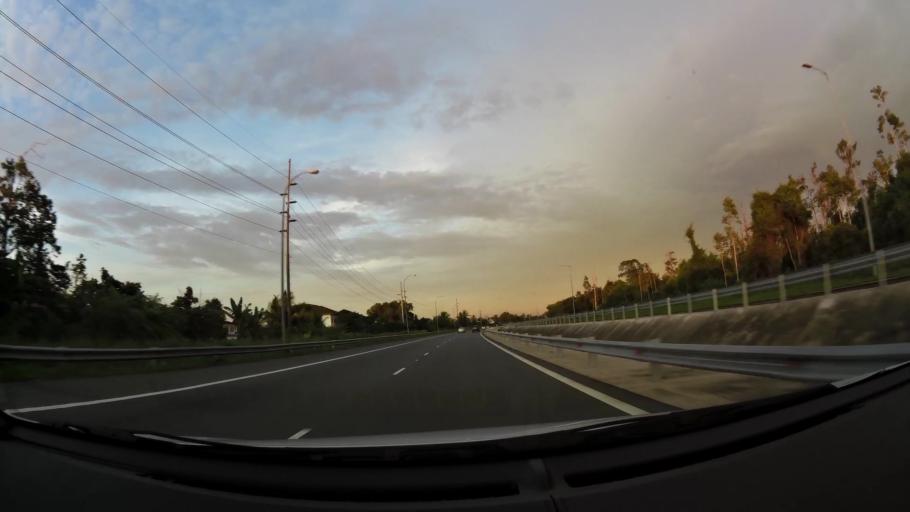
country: BN
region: Belait
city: Kuala Belait
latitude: 4.5791
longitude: 114.2359
